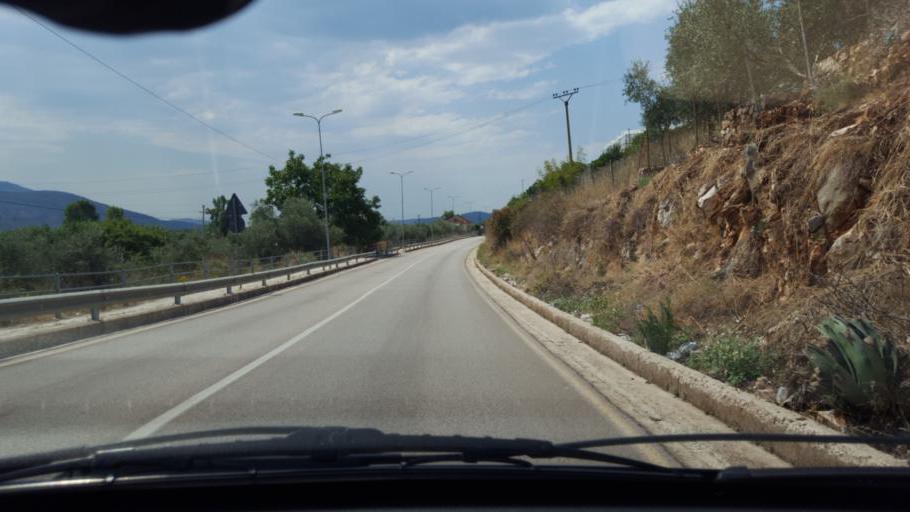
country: AL
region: Vlore
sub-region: Rrethi i Sarandes
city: Sarande
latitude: 39.8374
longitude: 20.0241
